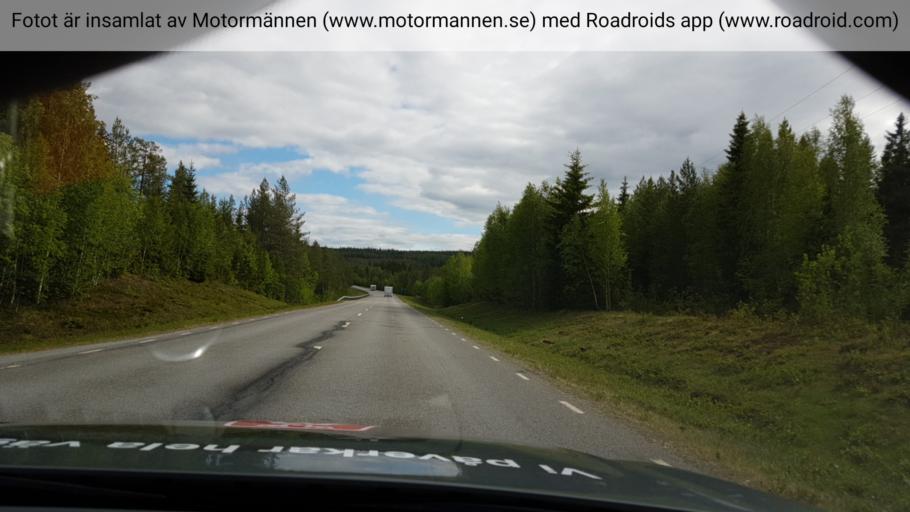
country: SE
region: Jaemtland
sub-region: Stroemsunds Kommun
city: Stroemsund
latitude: 64.2426
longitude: 15.4510
